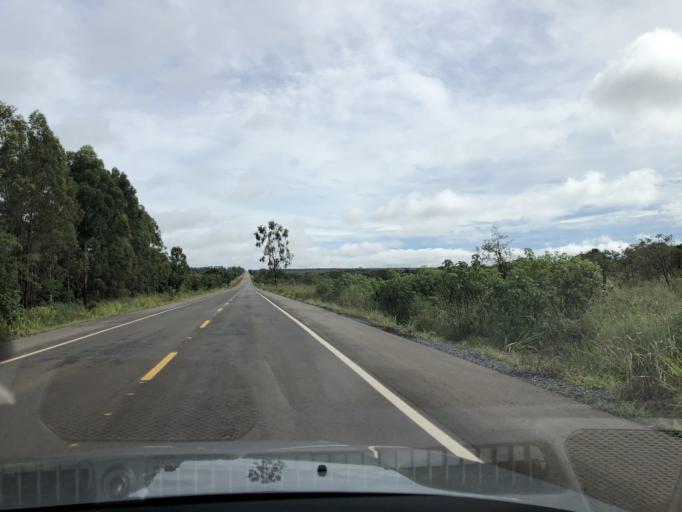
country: BR
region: Federal District
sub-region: Brasilia
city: Brasilia
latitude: -15.6685
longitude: -48.0871
